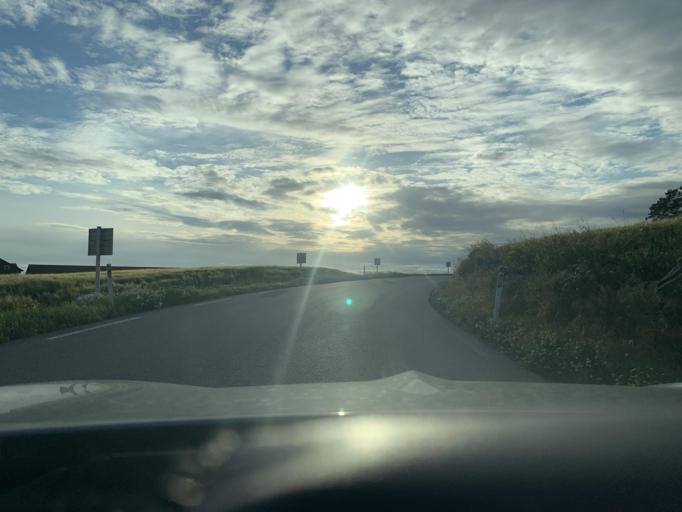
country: NO
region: Rogaland
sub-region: Time
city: Bryne
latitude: 58.7078
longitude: 5.6922
